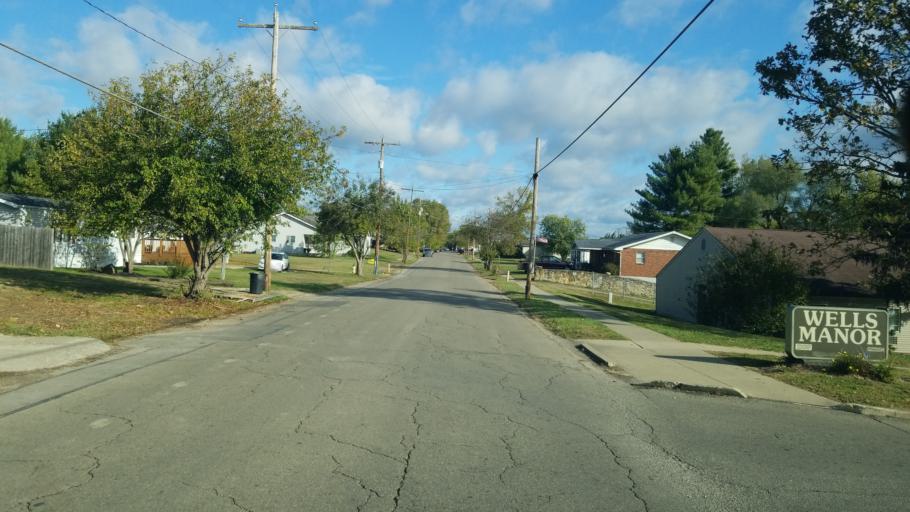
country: US
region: Ohio
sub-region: Jackson County
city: Wellston
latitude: 39.1185
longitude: -82.5388
